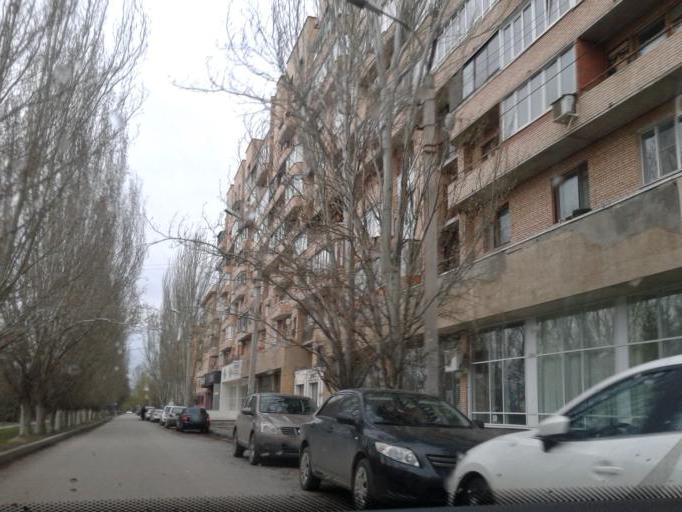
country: RU
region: Volgograd
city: Volgograd
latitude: 48.7123
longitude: 44.5311
